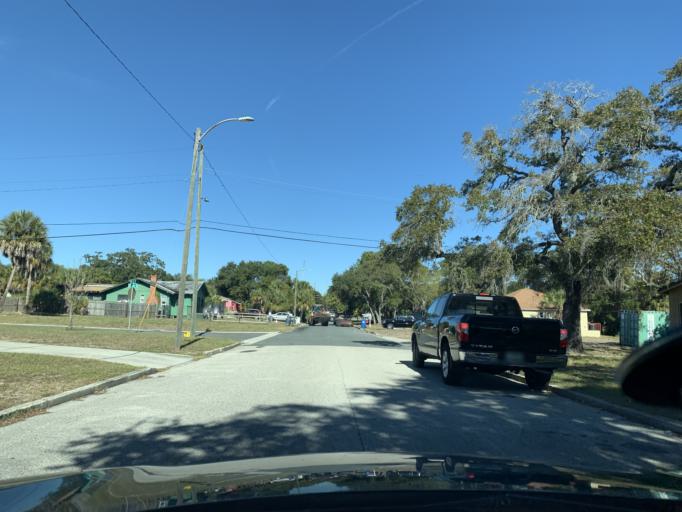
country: US
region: Florida
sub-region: Pinellas County
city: Gulfport
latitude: 27.7498
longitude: -82.6900
